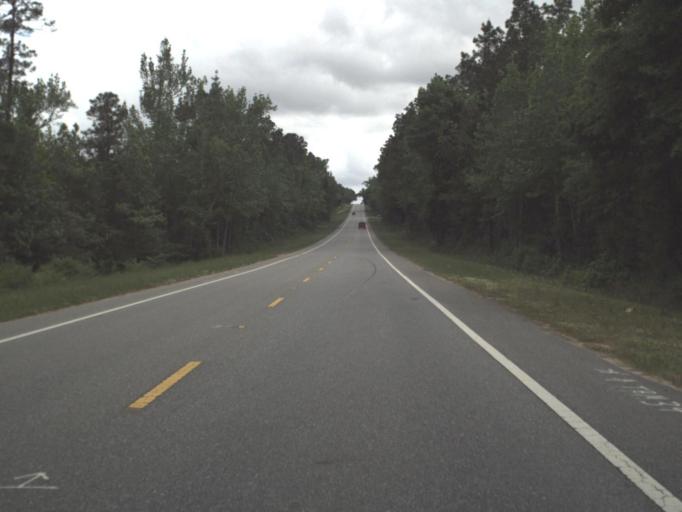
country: US
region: Florida
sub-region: Santa Rosa County
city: Point Baker
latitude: 30.7880
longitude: -87.0415
